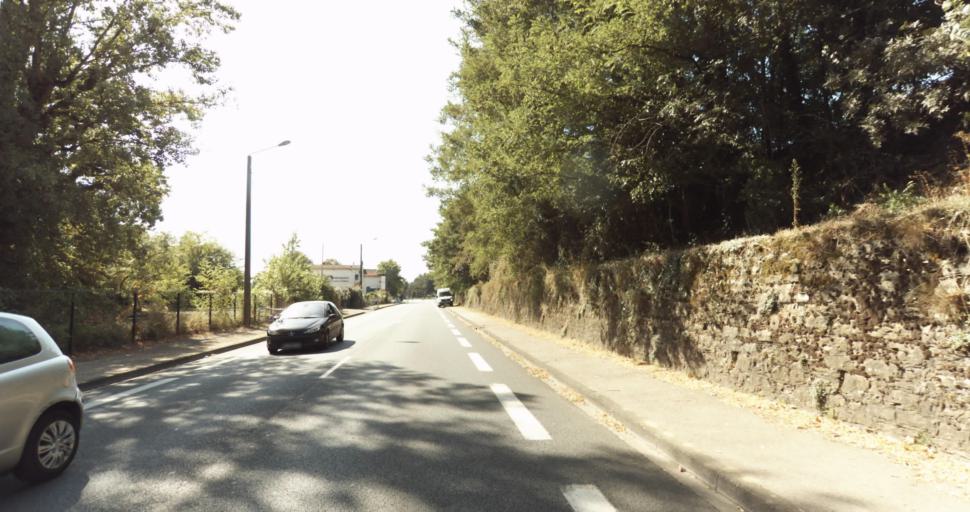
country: FR
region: Rhone-Alpes
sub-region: Departement du Rhone
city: Albigny-sur-Saone
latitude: 45.8677
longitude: 4.8345
